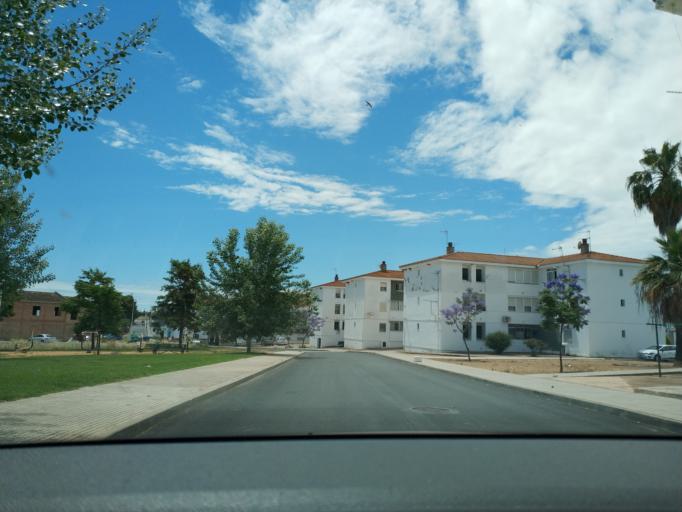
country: ES
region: Andalusia
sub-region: Provincia de Huelva
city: Cartaya
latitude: 37.2849
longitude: -7.1468
